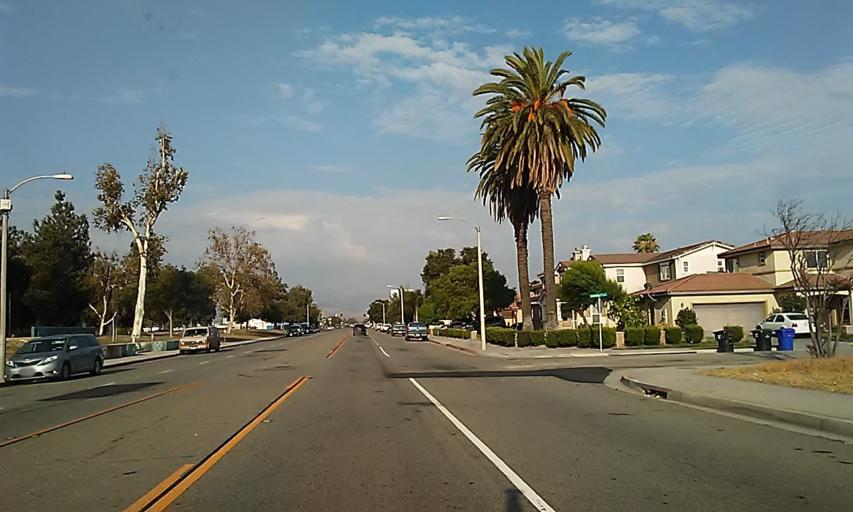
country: US
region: California
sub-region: San Bernardino County
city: San Bernardino
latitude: 34.1083
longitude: -117.2830
